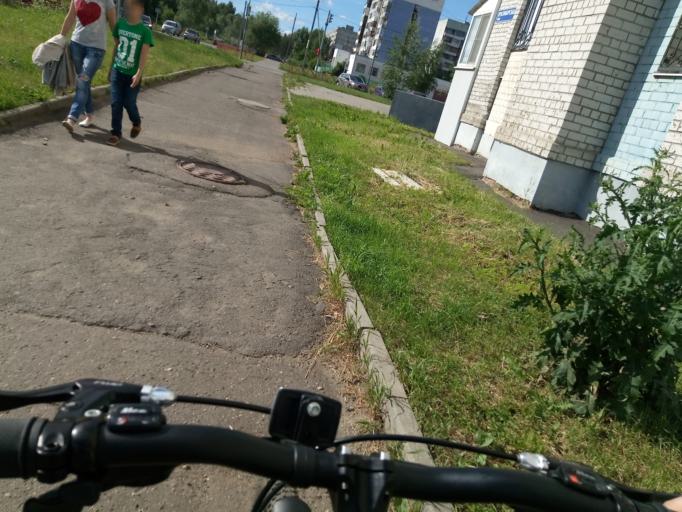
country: RU
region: Jaroslavl
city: Yaroslavl
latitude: 57.6411
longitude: 39.9465
